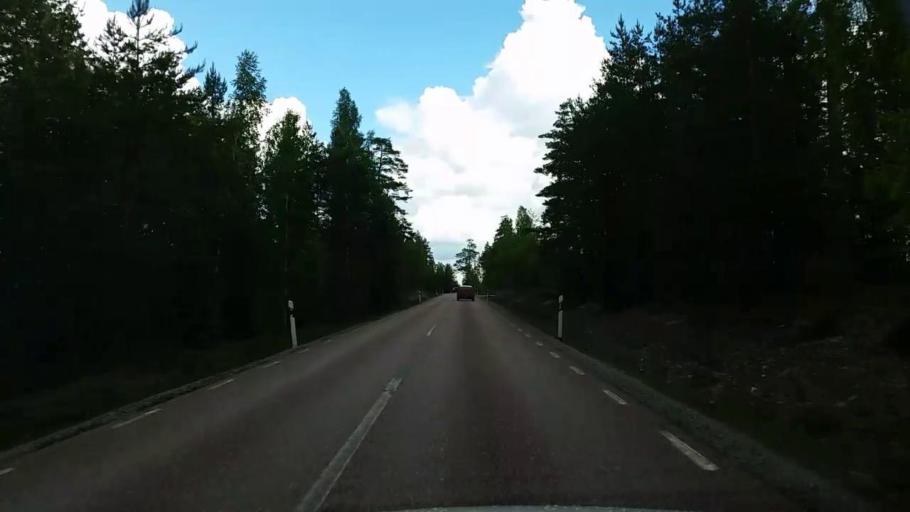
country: SE
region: Vaestmanland
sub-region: Fagersta Kommun
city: Fagersta
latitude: 59.8656
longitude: 15.8422
